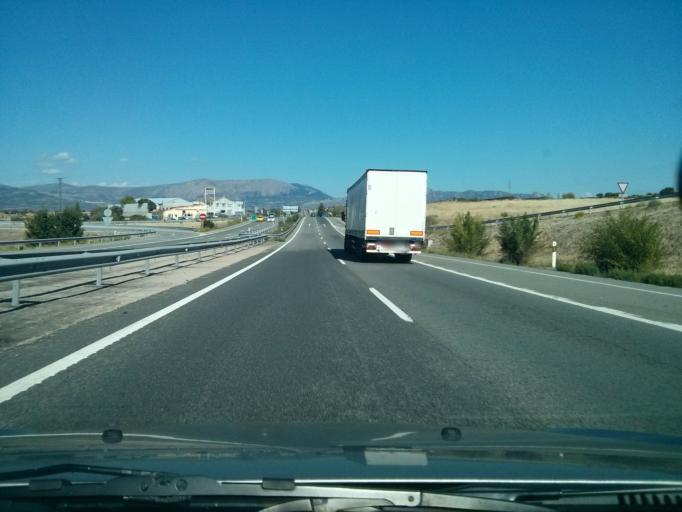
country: ES
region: Madrid
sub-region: Provincia de Madrid
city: Pedrezuela
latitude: 40.7654
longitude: -3.6043
